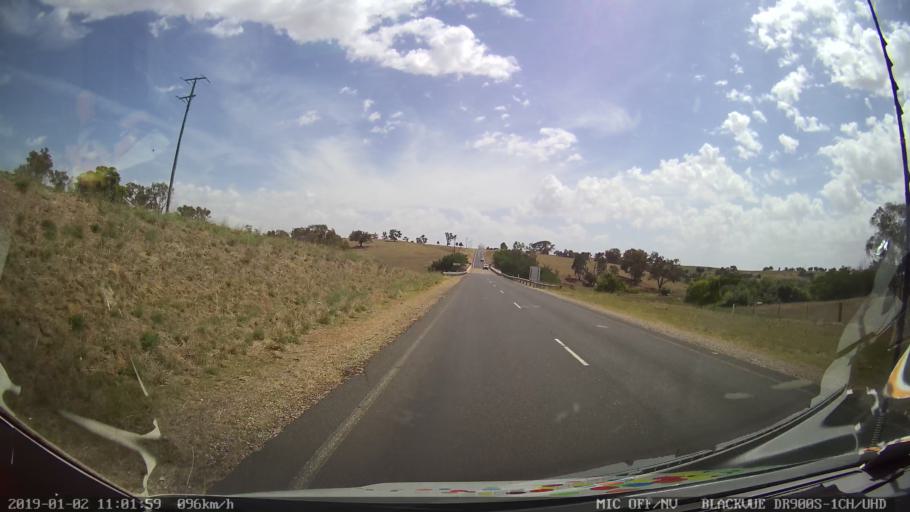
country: AU
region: New South Wales
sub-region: Young
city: Young
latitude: -34.5913
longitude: 148.3237
